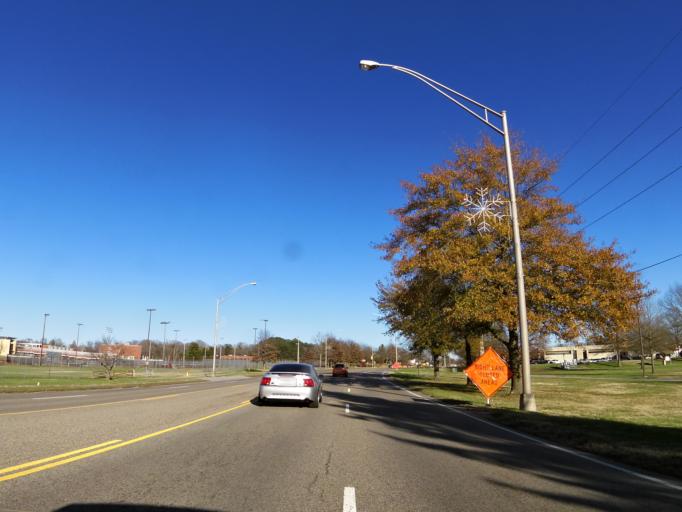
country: US
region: Tennessee
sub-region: Anderson County
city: Oak Ridge
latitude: 36.0129
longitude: -84.2634
